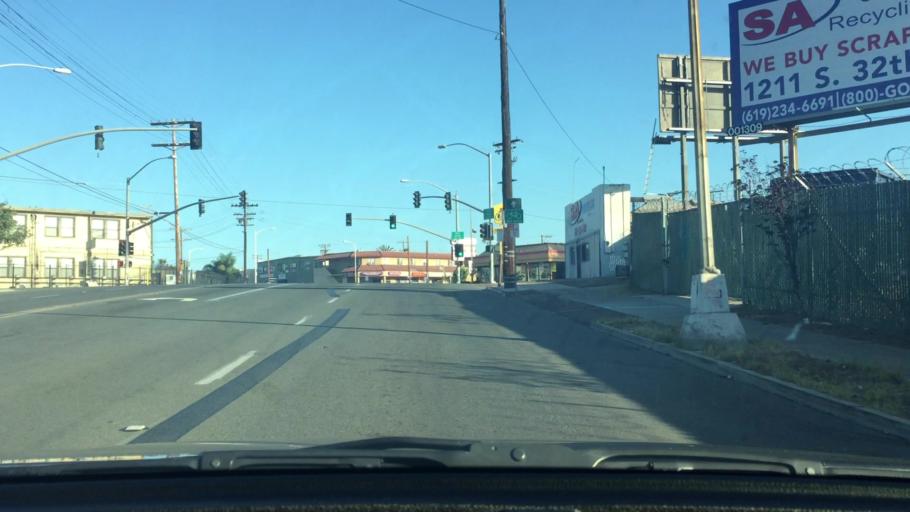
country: US
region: California
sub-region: San Diego County
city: National City
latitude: 32.6921
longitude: -117.1249
